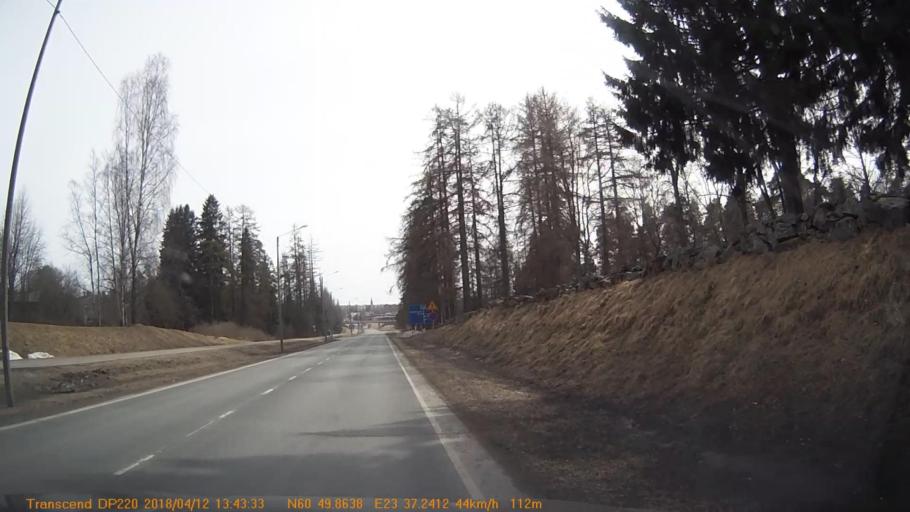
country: FI
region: Haeme
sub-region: Forssa
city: Forssa
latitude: 60.8307
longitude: 23.6209
